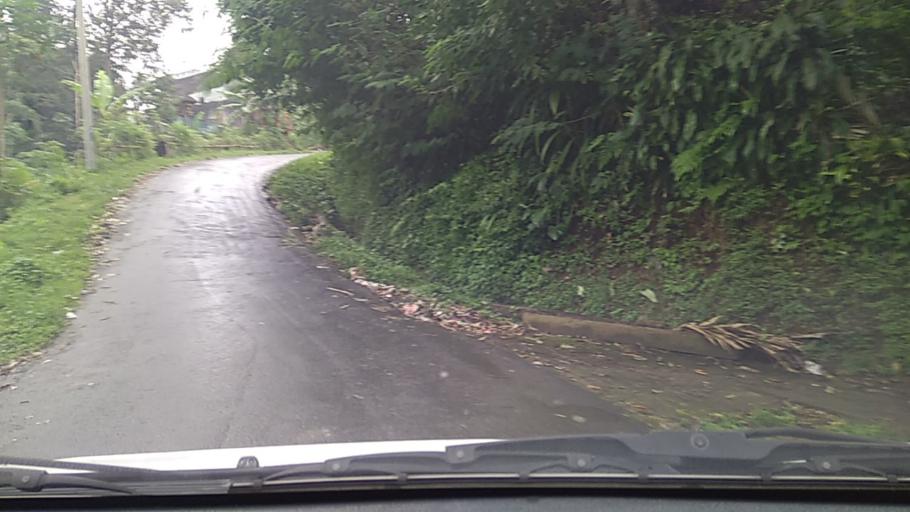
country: ID
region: Bali
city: Banjar Padangbulia
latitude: -8.1938
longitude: 115.1838
